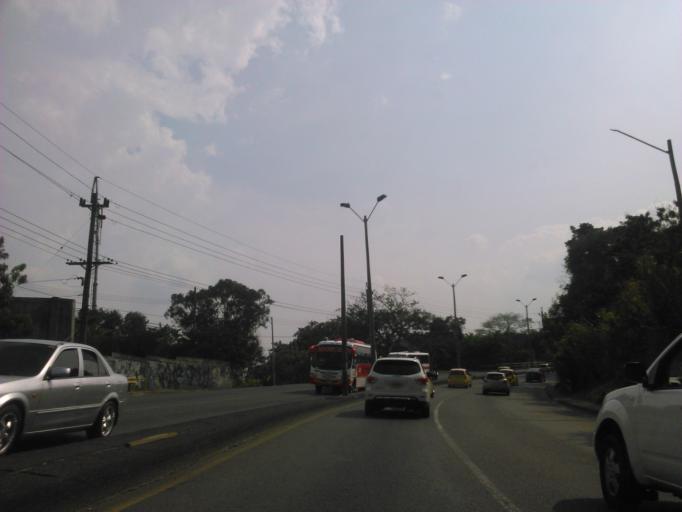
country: CO
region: Antioquia
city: Bello
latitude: 6.3042
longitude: -75.5606
